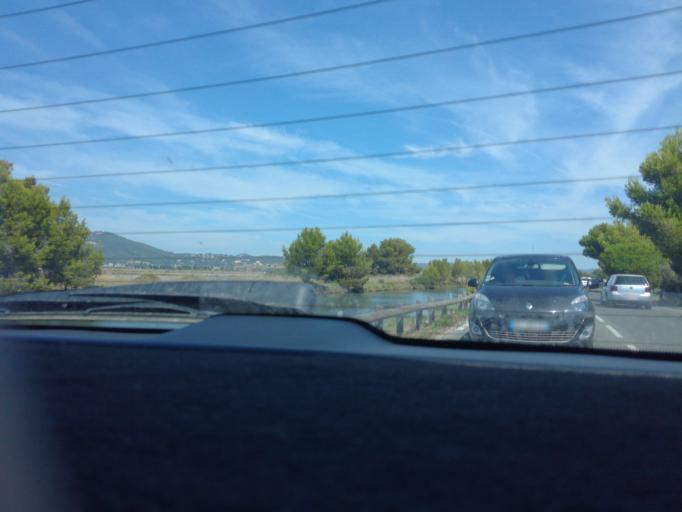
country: FR
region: Provence-Alpes-Cote d'Azur
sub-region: Departement du Var
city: Hyeres
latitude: 43.0682
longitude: 6.1474
